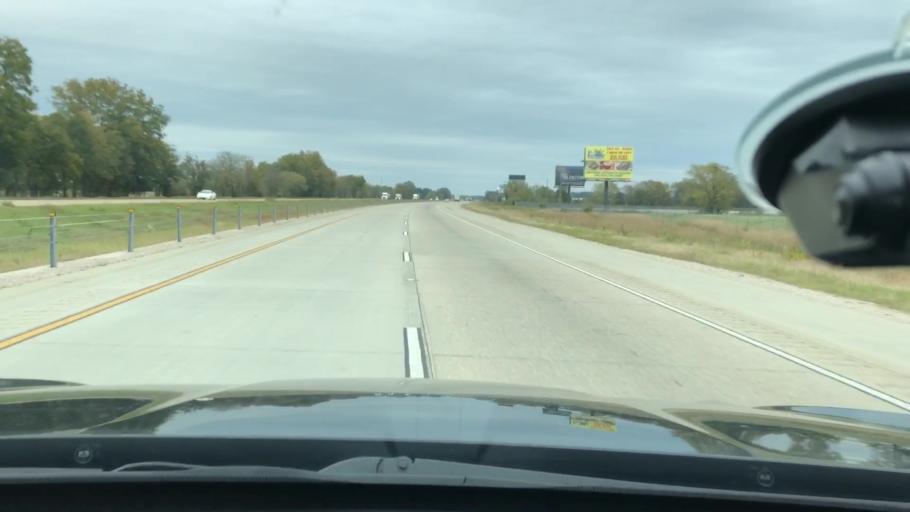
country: US
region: Arkansas
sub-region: Miller County
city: Texarkana
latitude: 33.5325
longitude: -93.9186
